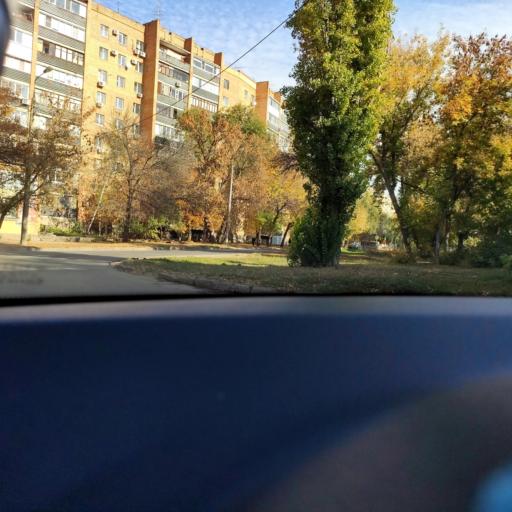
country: RU
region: Samara
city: Samara
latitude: 53.1947
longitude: 50.1346
